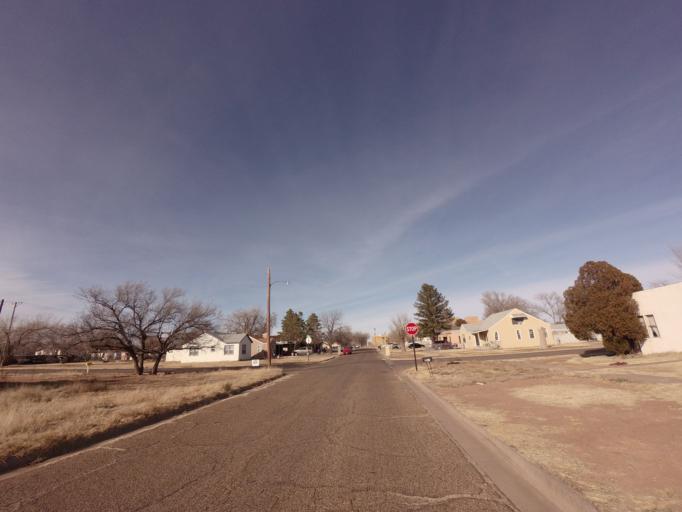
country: US
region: New Mexico
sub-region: Curry County
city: Clovis
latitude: 34.4086
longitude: -103.2155
